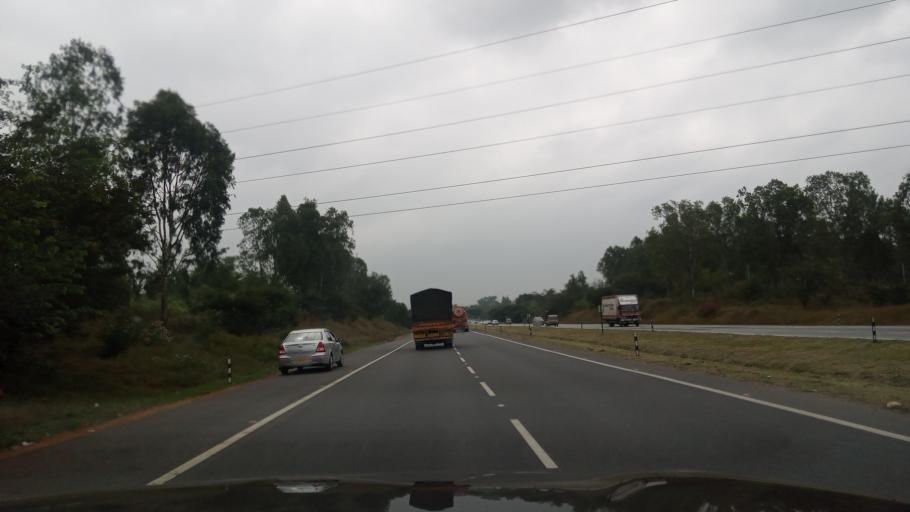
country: IN
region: Karnataka
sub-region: Bangalore Rural
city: Nelamangala
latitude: 13.0352
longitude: 77.4761
